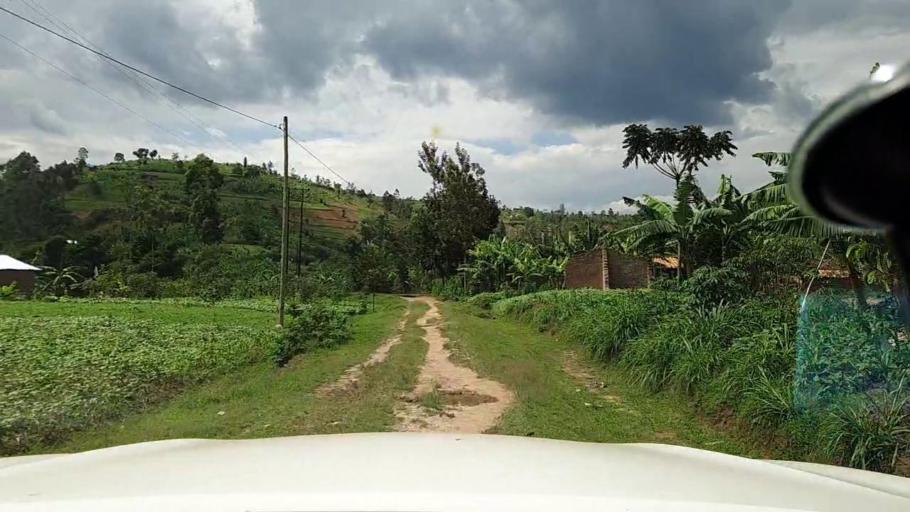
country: RW
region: Southern Province
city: Gitarama
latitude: -1.8269
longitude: 29.8031
